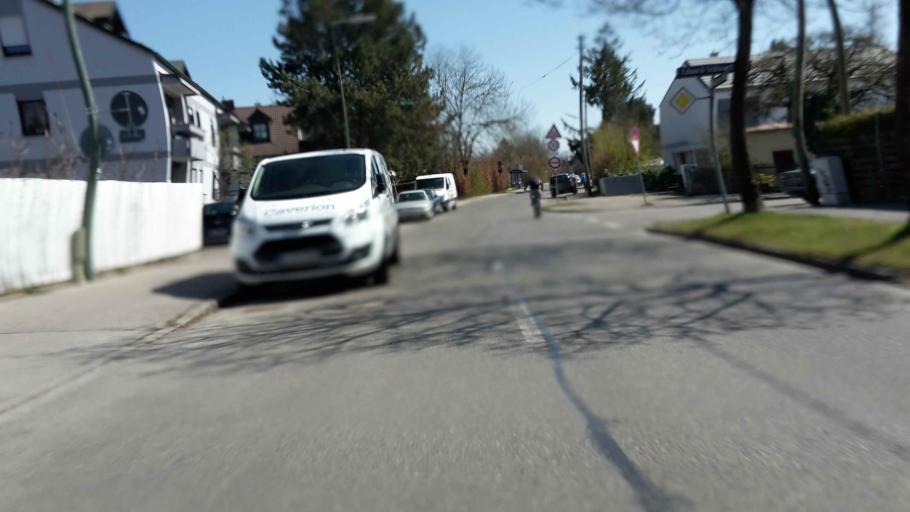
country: DE
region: Bavaria
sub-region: Upper Bavaria
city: Karlsfeld
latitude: 48.1821
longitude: 11.4736
